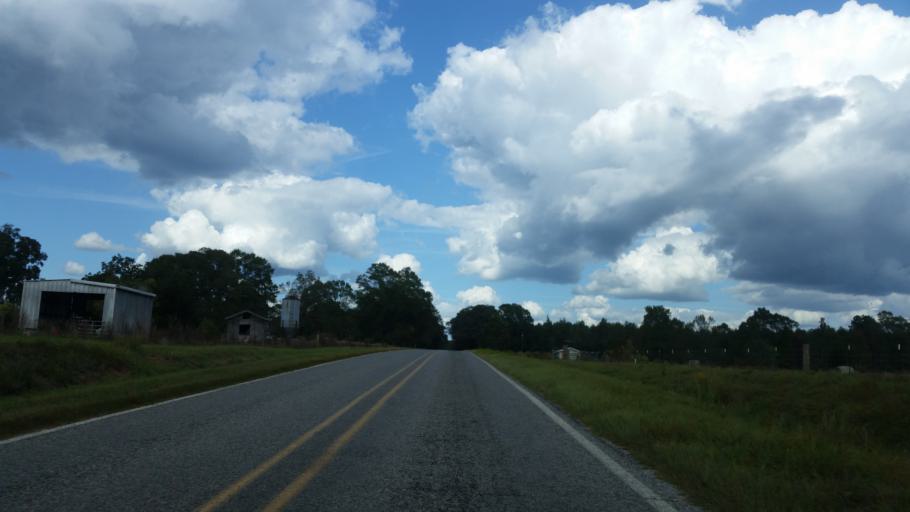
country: US
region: Mississippi
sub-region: Stone County
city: Wiggins
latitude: 30.9333
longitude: -89.0561
